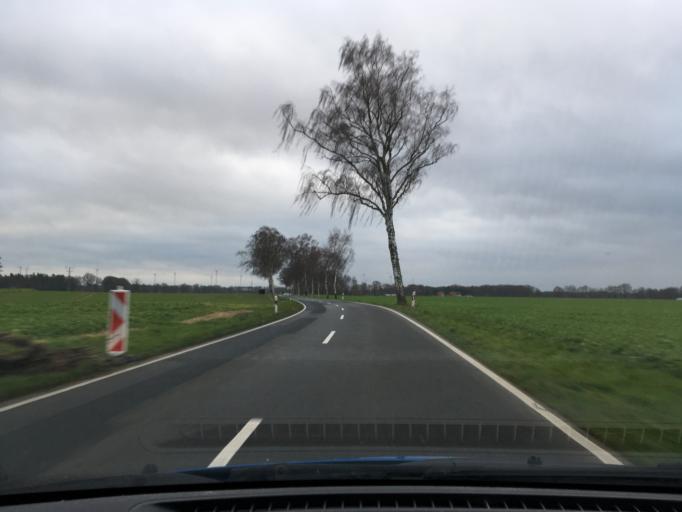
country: DE
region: Lower Saxony
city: Ebstorf
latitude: 53.0128
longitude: 10.4190
